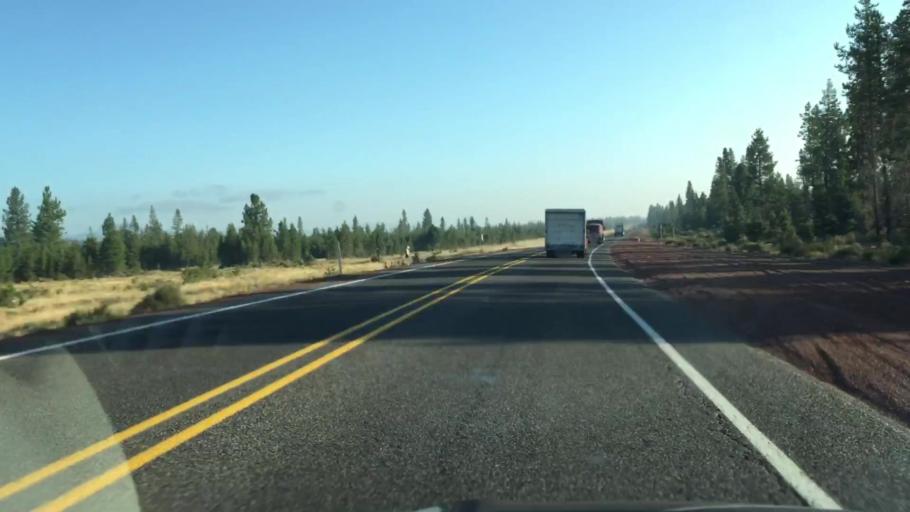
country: US
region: Oregon
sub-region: Deschutes County
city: La Pine
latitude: 43.4289
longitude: -121.7153
